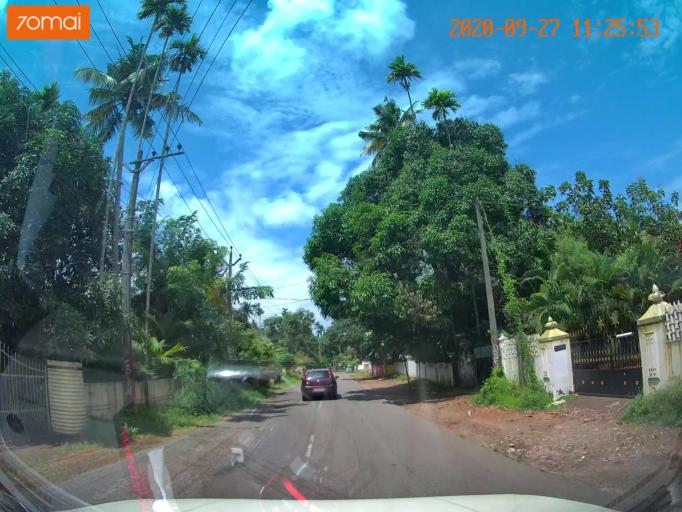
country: IN
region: Kerala
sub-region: Thrissur District
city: Thanniyam
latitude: 10.4146
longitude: 76.1552
